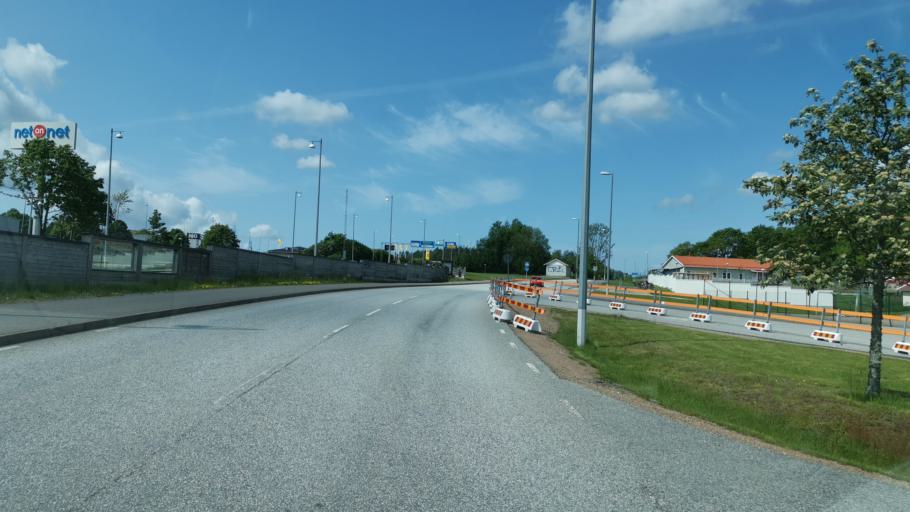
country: SE
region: Vaestra Goetaland
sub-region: Uddevalla Kommun
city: Uddevalla
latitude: 58.3509
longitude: 11.8357
